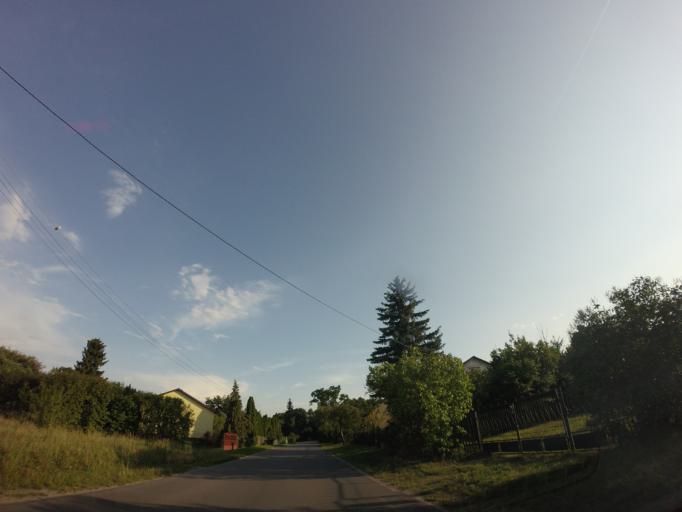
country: PL
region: Lublin Voivodeship
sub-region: Powiat pulawski
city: Kurow
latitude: 51.4216
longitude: 22.2287
